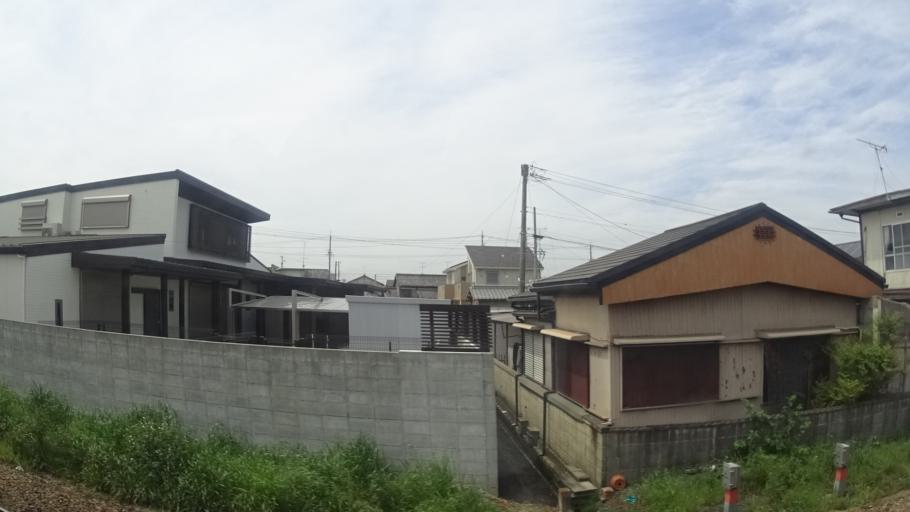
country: JP
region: Mie
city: Hisai-motomachi
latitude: 34.5839
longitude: 136.5273
